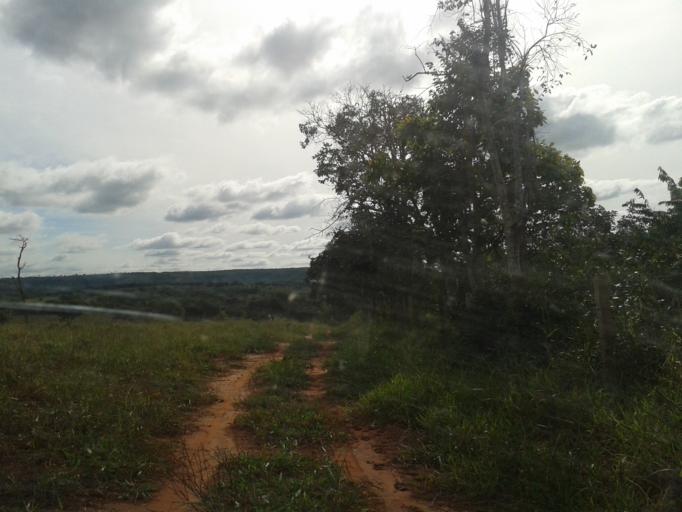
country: BR
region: Minas Gerais
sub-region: Campina Verde
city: Campina Verde
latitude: -19.4281
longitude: -49.7261
